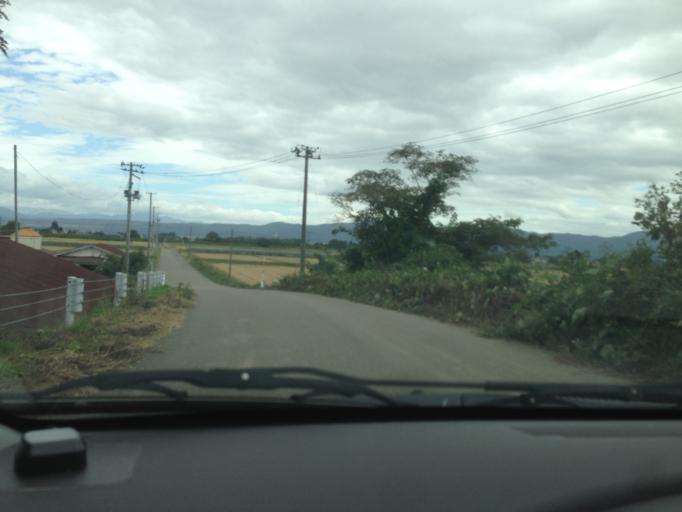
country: JP
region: Fukushima
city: Kitakata
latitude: 37.4937
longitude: 139.8342
